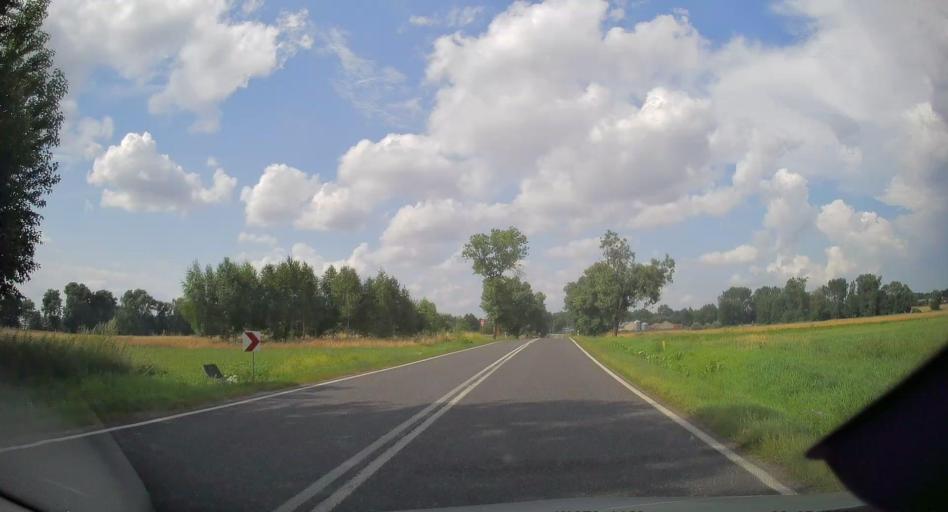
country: PL
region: Lodz Voivodeship
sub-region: Powiat brzezinski
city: Jezow
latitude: 51.8039
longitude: 20.0151
